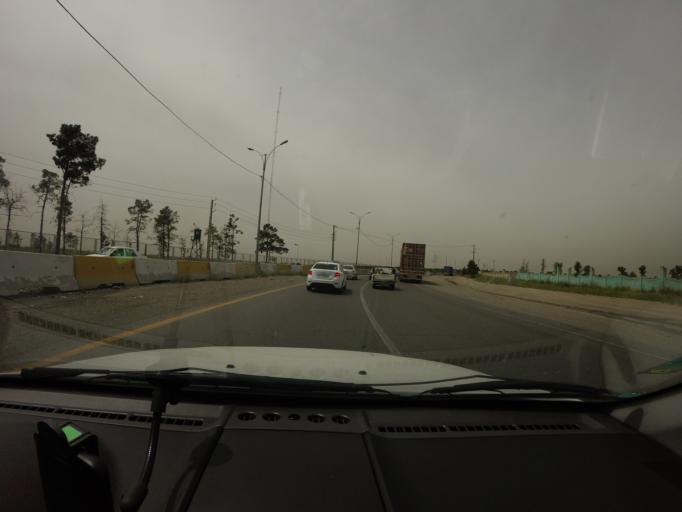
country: IR
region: Tehran
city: Eslamshahr
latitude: 35.5951
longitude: 51.2468
